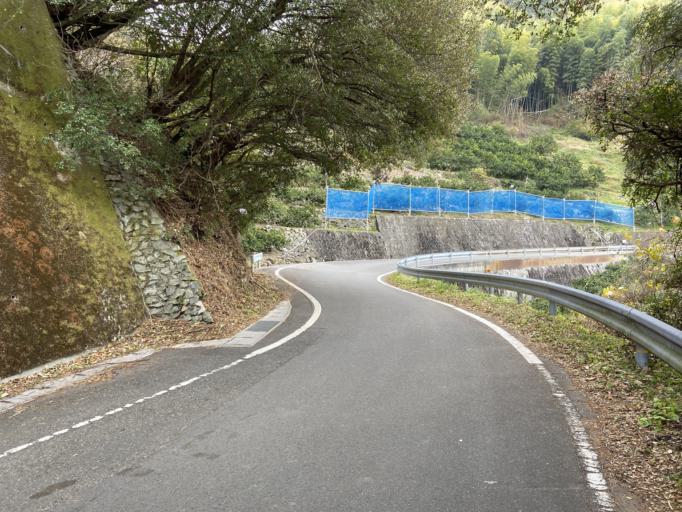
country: JP
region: Ehime
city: Uwajima
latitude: 33.2600
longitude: 132.5418
